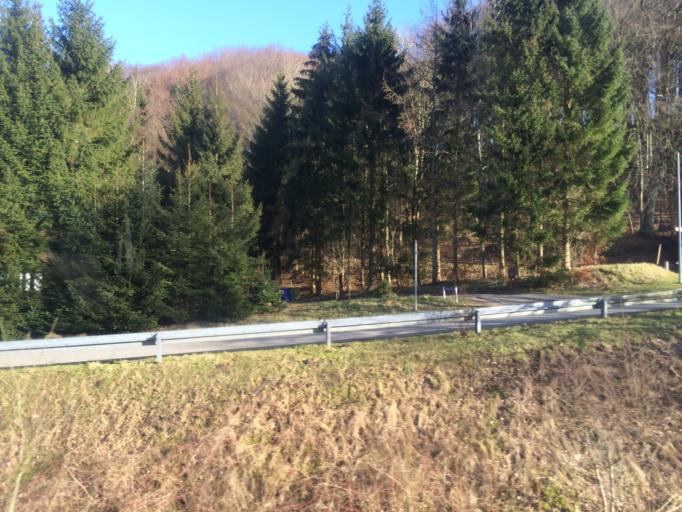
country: DK
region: South Denmark
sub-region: Vejle Kommune
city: Vejle
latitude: 55.7565
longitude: 9.5323
